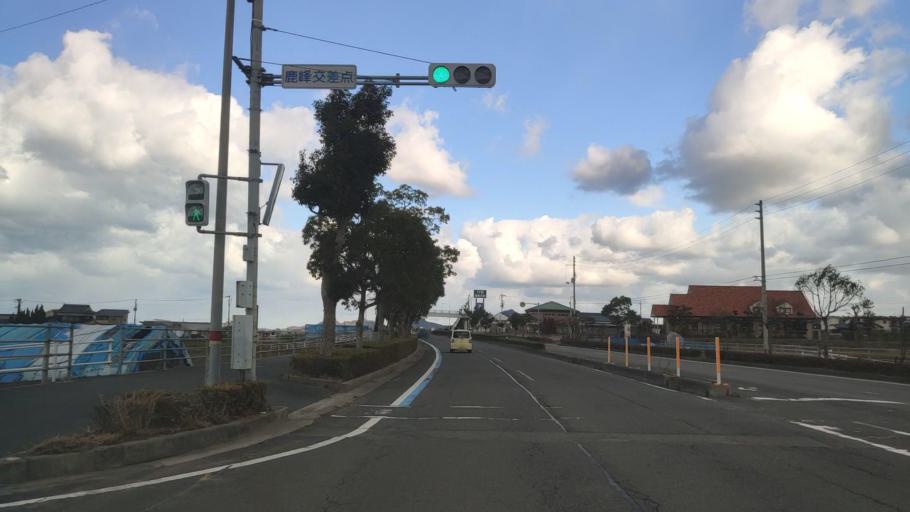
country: JP
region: Ehime
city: Hojo
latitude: 33.9381
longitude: 132.7733
